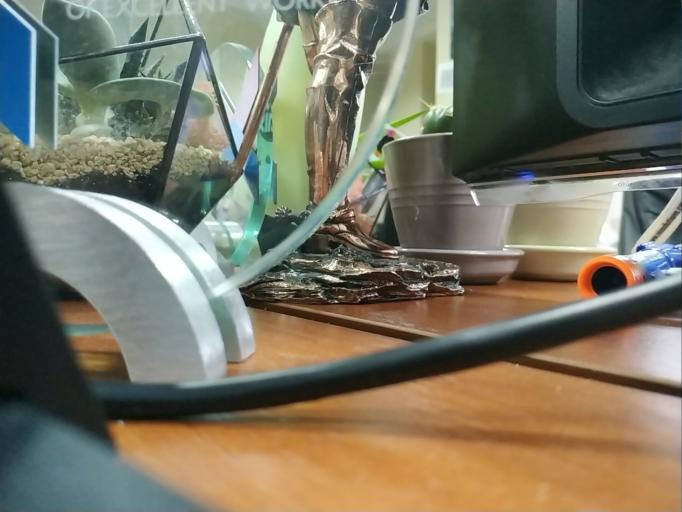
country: RU
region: Moskovskaya
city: Nekrasovskiy
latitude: 56.0855
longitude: 37.4593
